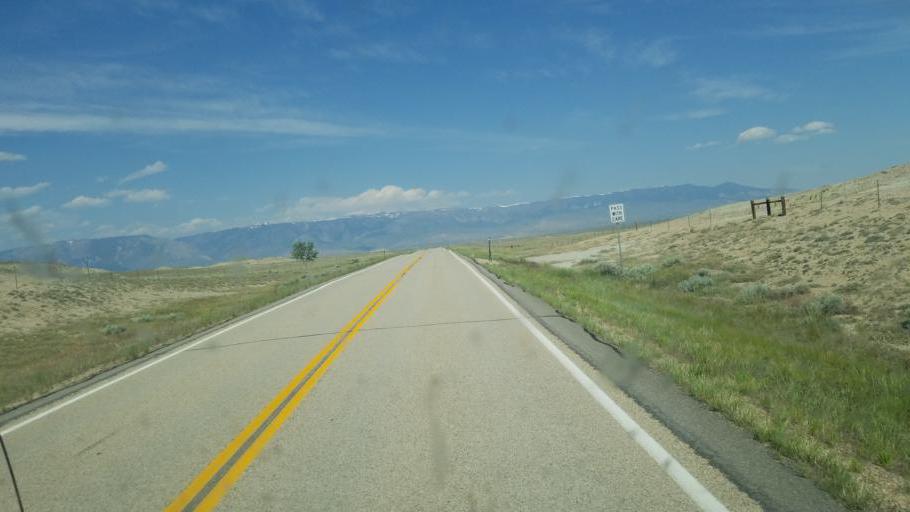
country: US
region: Wyoming
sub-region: Park County
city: Powell
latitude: 44.8428
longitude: -108.9930
